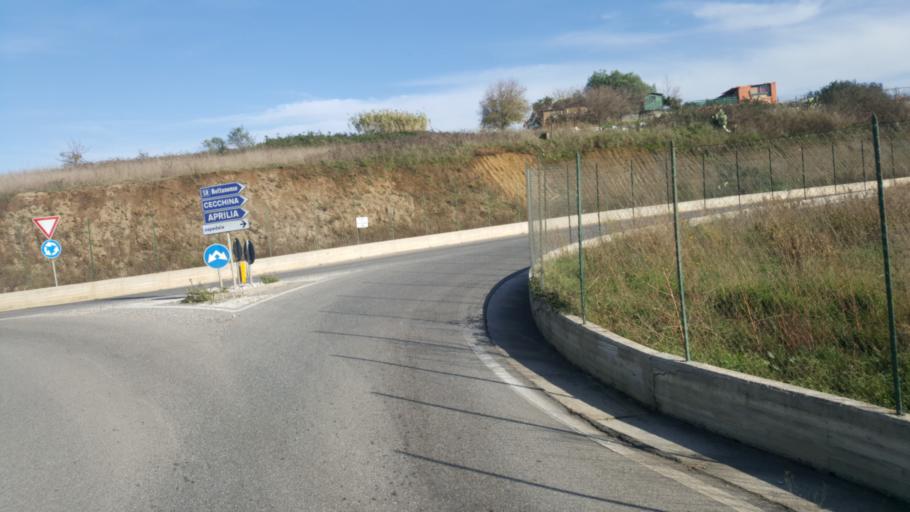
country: IT
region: Latium
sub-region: Citta metropolitana di Roma Capitale
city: Mantiglia di Ardea
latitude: 41.6729
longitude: 12.6332
